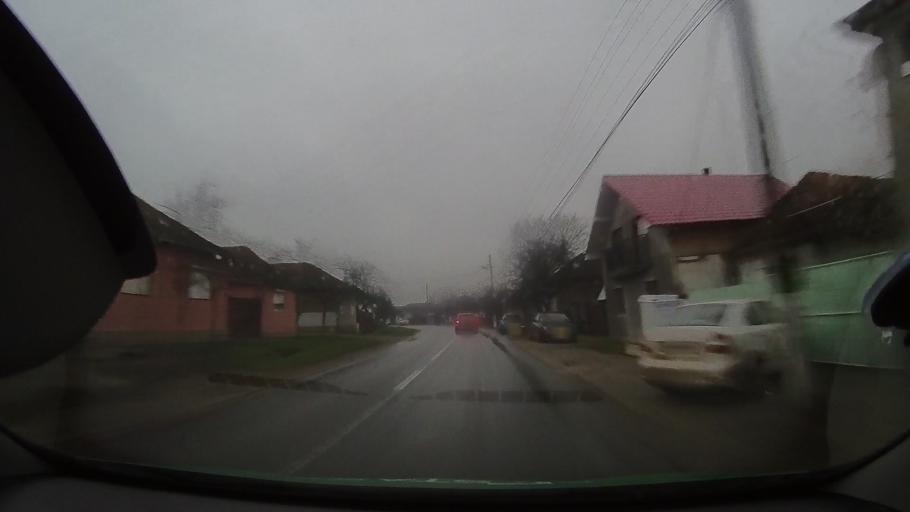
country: RO
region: Arad
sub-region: Comuna Craiova
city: Craiova
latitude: 46.5875
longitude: 21.9752
